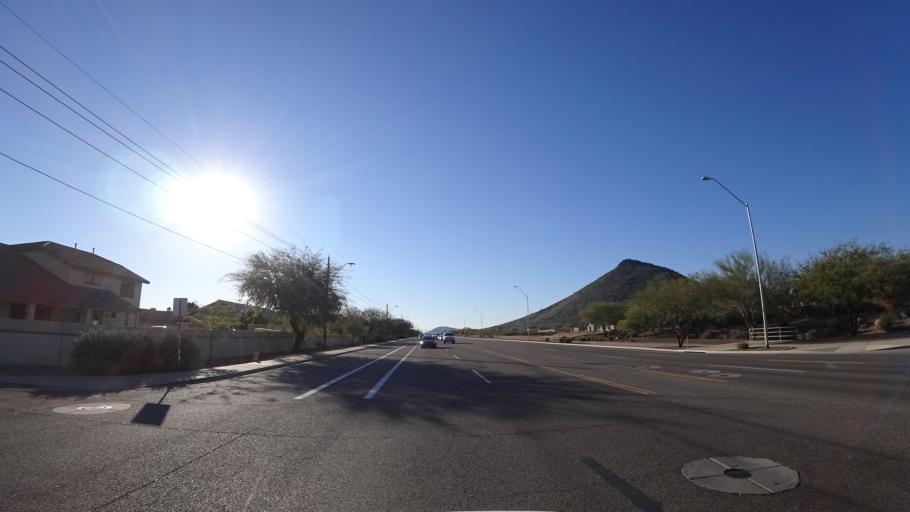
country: US
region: Arizona
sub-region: Maricopa County
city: Peoria
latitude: 33.7124
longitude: -112.1744
